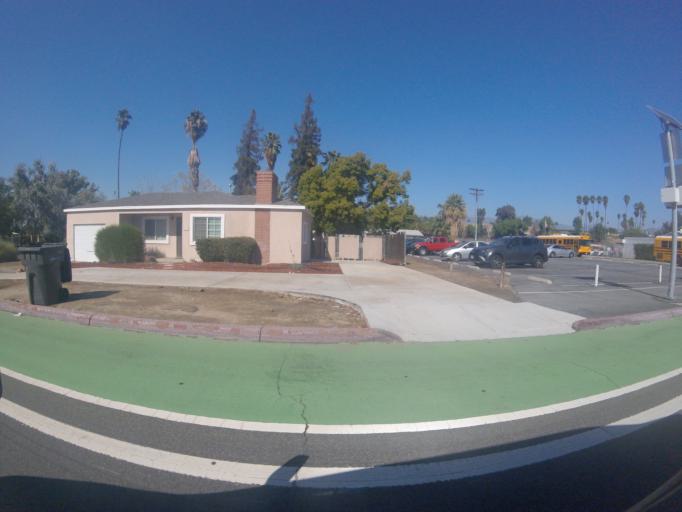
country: US
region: California
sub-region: San Bernardino County
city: Redlands
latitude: 34.0555
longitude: -117.1693
